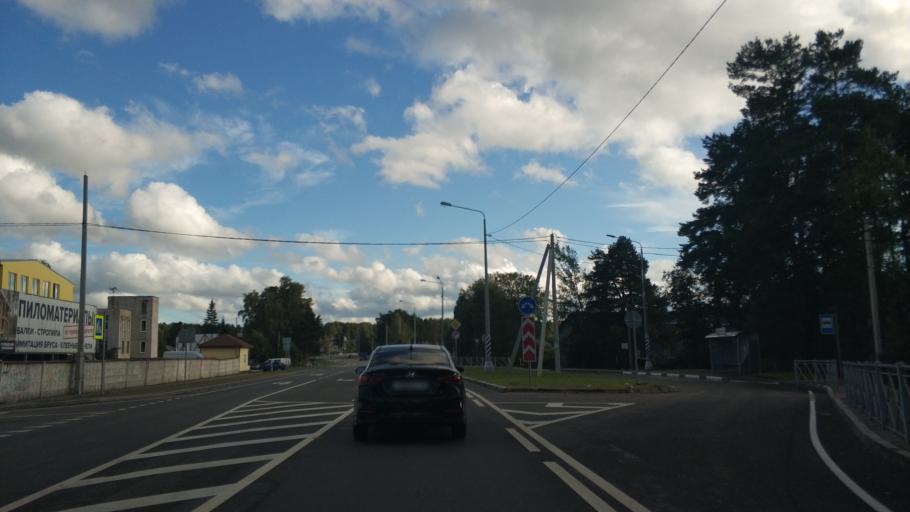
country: RU
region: Leningrad
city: Priozersk
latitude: 61.0026
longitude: 30.1810
